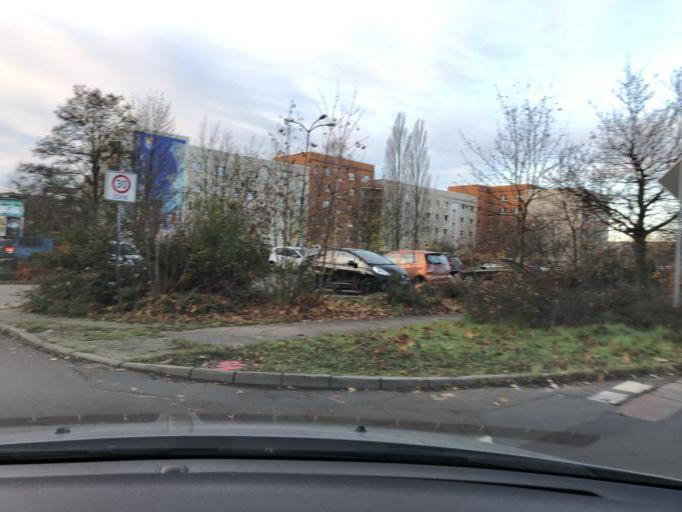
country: DE
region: Saxony-Anhalt
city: Schkopau
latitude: 51.4449
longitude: 11.9686
